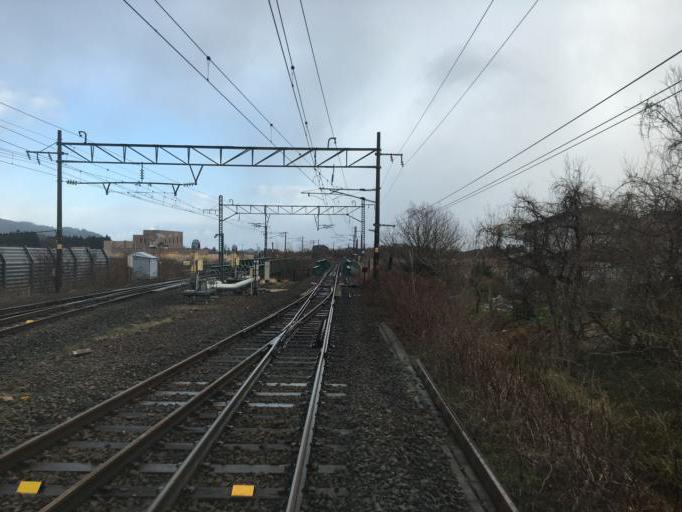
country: JP
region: Aomori
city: Aomori Shi
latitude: 40.9306
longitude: 140.9575
